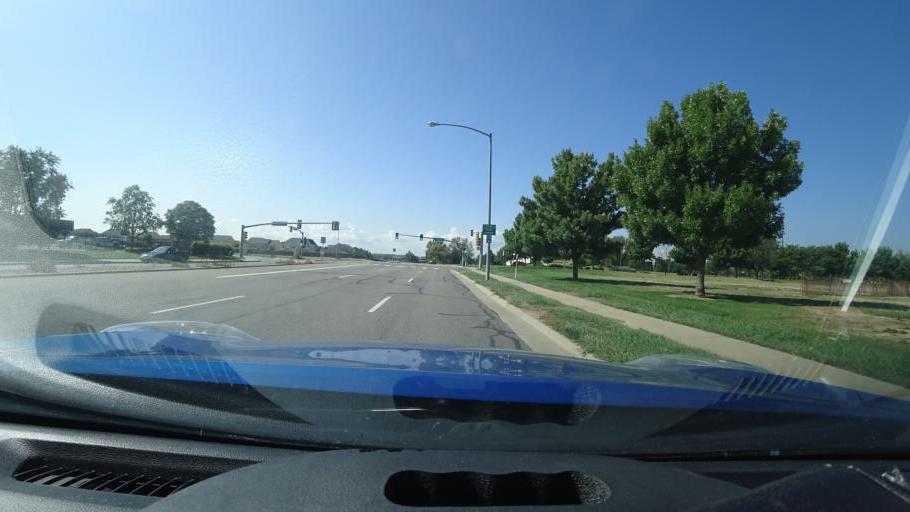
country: US
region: Colorado
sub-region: Adams County
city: Aurora
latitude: 39.7174
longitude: -104.7913
